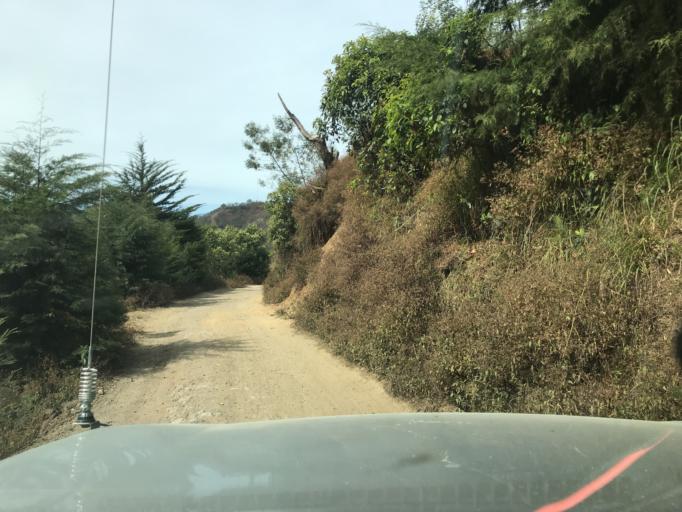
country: TL
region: Ainaro
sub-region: Ainaro
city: Ainaro
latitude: -8.8831
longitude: 125.5437
